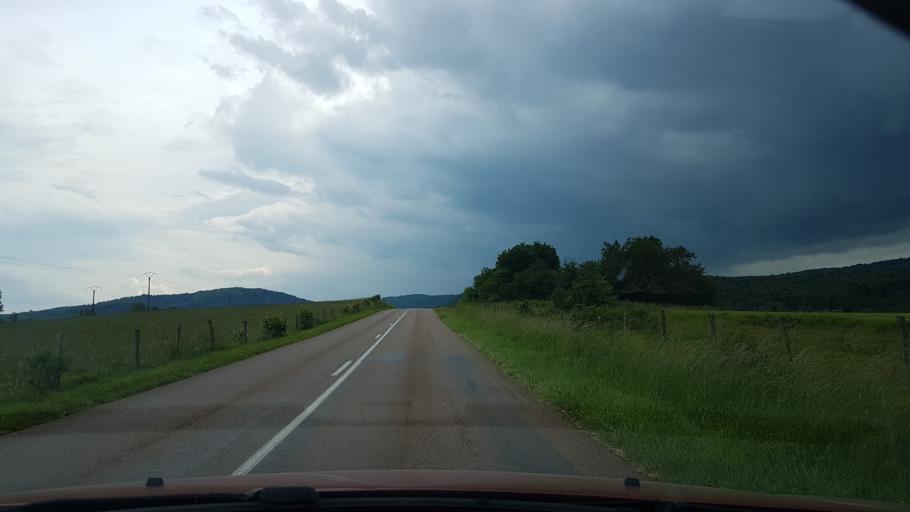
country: FR
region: Franche-Comte
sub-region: Departement du Jura
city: Clairvaux-les-Lacs
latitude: 46.5737
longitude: 5.6826
